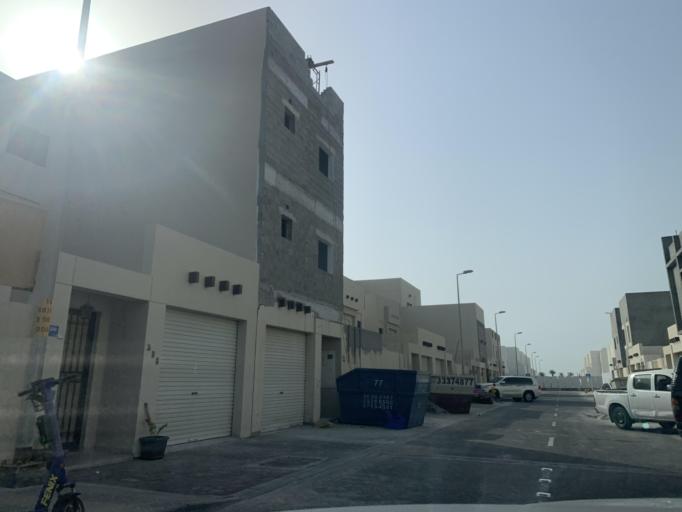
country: BH
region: Manama
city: Jidd Hafs
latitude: 26.2296
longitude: 50.4473
